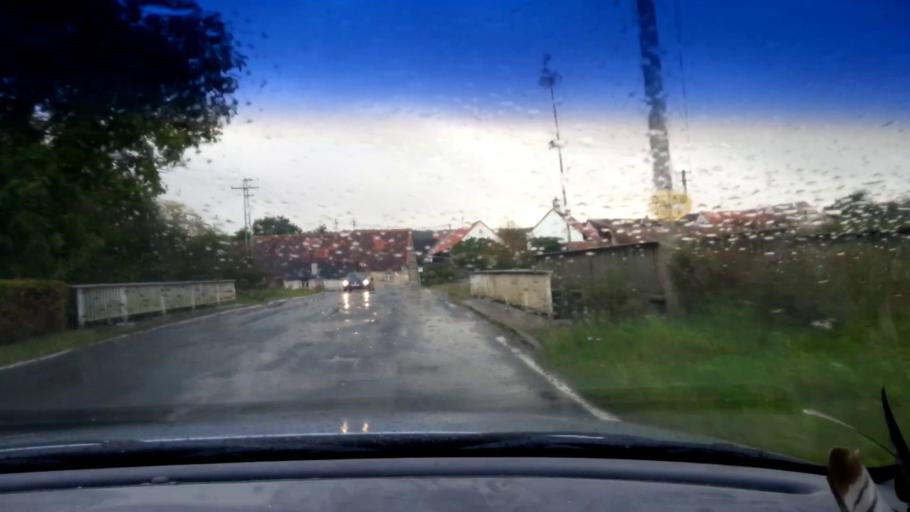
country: DE
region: Bavaria
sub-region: Upper Franconia
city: Burgebrach
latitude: 49.8467
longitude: 10.7324
